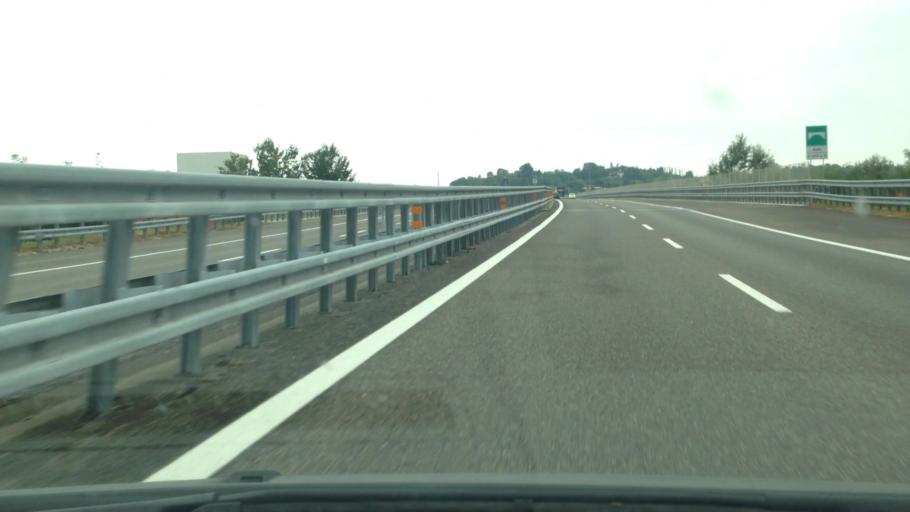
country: IT
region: Piedmont
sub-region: Provincia di Asti
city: Asti
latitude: 44.9127
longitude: 8.2332
